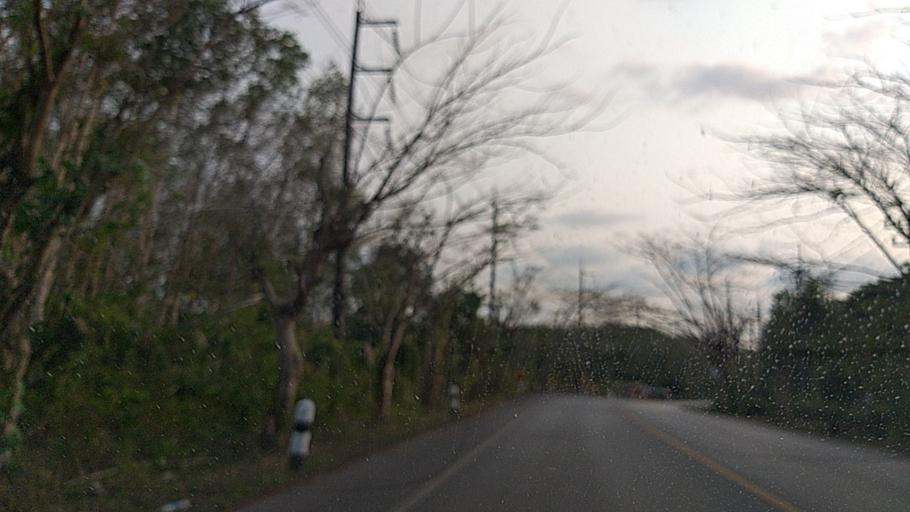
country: TH
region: Trat
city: Khao Saming
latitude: 12.2919
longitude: 102.3314
